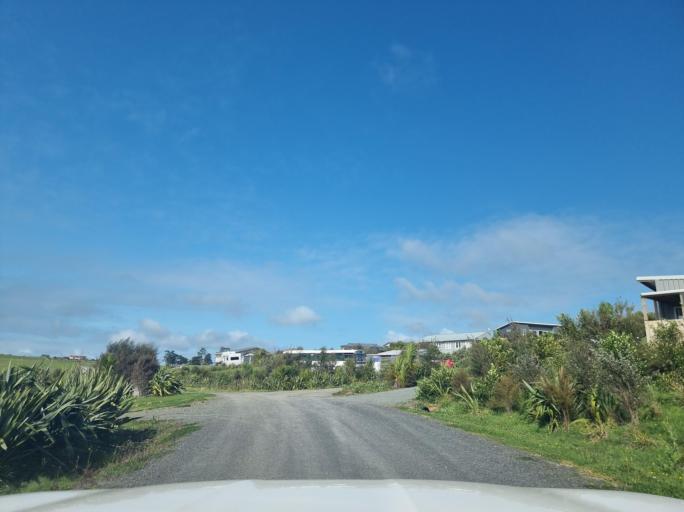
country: NZ
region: Auckland
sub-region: Auckland
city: Wellsford
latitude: -36.1386
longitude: 174.4937
